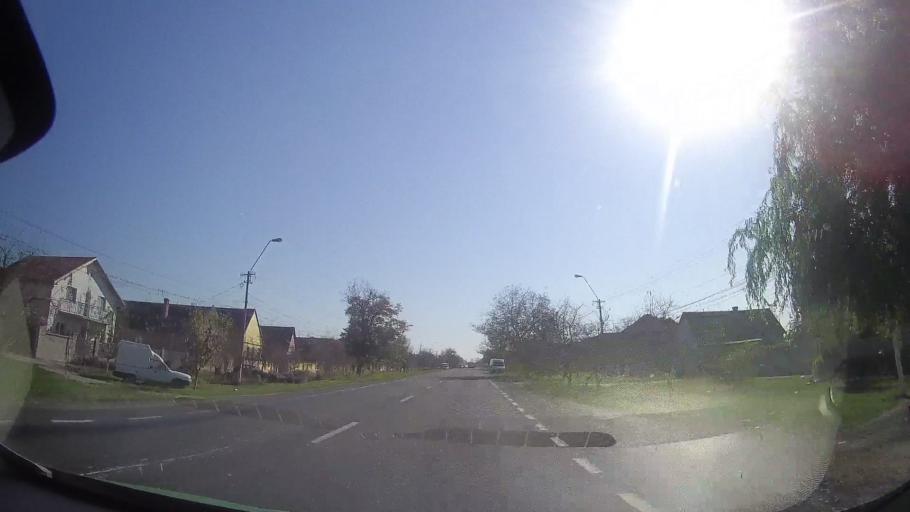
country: RO
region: Timis
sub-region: Comuna Belint
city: Belint
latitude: 45.7524
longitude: 21.7602
